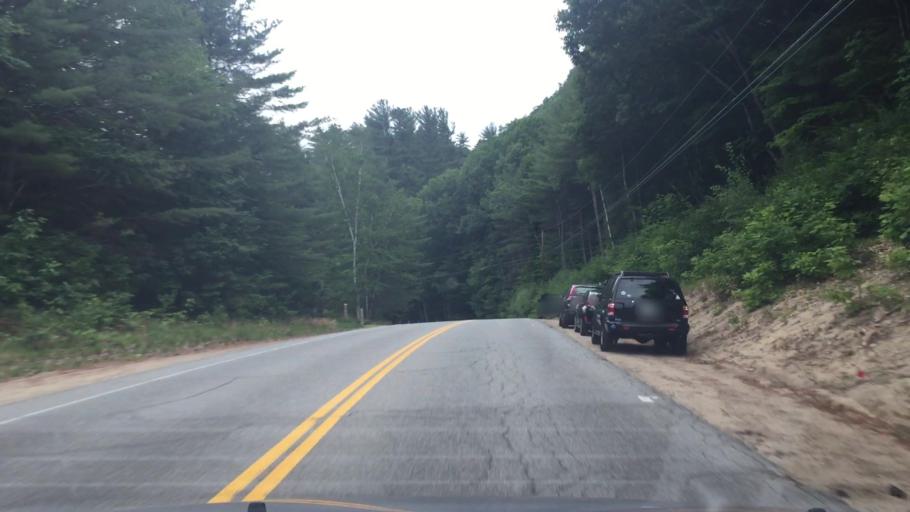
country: US
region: New Hampshire
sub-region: Carroll County
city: North Conway
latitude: 44.0859
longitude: -71.1645
